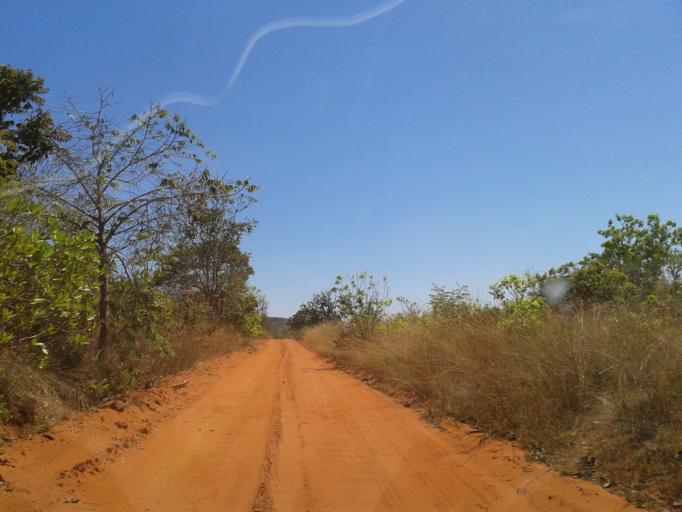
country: BR
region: Minas Gerais
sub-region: Ituiutaba
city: Ituiutaba
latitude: -19.1097
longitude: -49.2833
